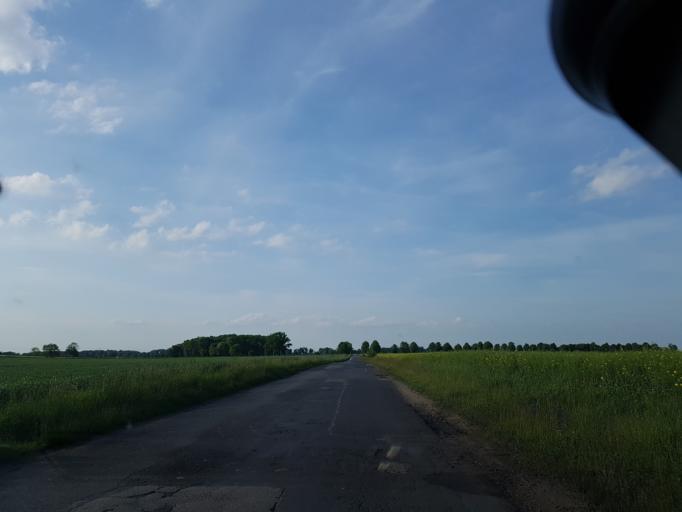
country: PL
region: Lower Silesian Voivodeship
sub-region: Powiat wroclawski
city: Zorawina
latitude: 50.9126
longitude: 17.0026
